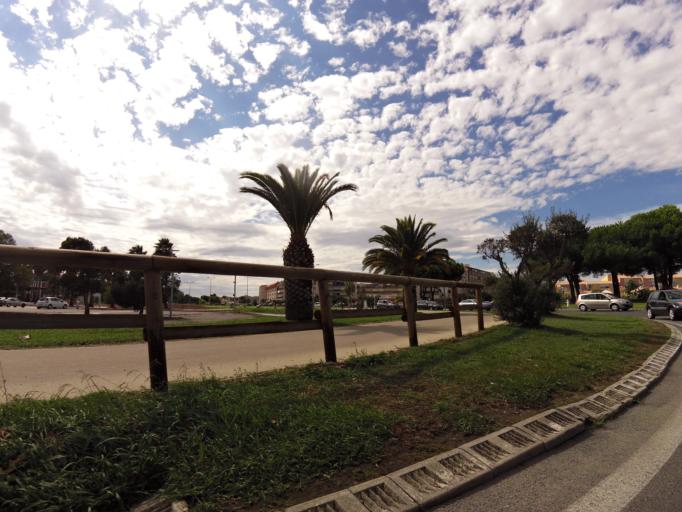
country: FR
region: Languedoc-Roussillon
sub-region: Departement du Gard
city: Le Grau-du-Roi
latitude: 43.5259
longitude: 4.1502
